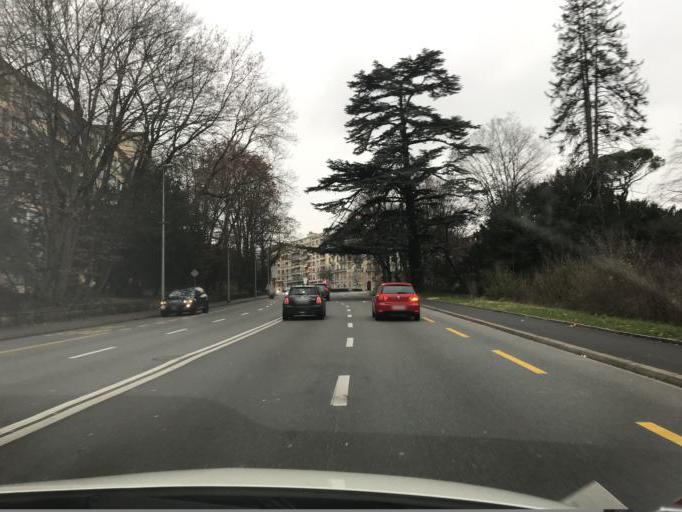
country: CH
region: Geneva
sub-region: Geneva
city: Geneve
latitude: 46.2176
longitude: 6.1504
